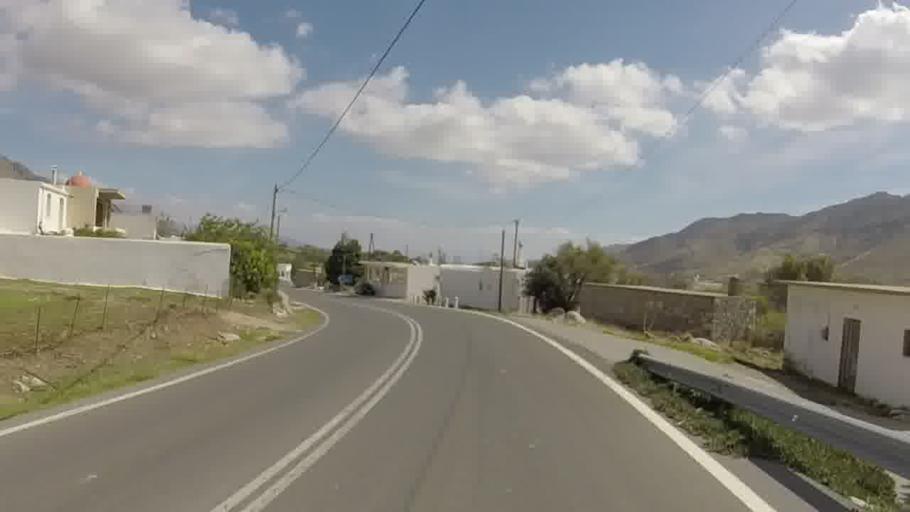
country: GR
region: Crete
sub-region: Nomos Rethymnis
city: Agia Galini
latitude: 35.1505
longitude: 24.6254
